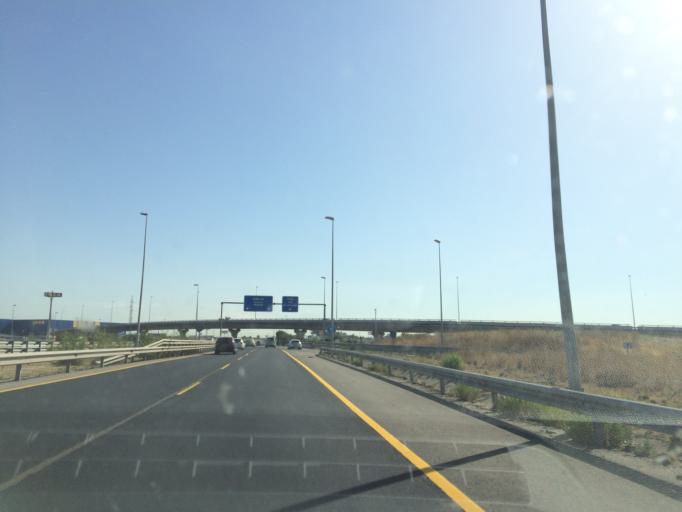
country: ES
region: Madrid
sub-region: Provincia de Madrid
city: Mostoles
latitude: 40.3441
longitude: -3.8612
